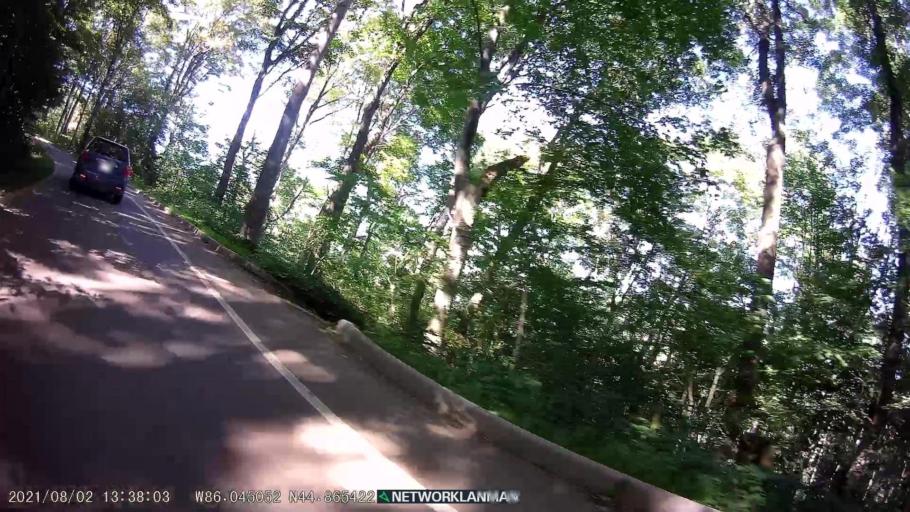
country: US
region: Michigan
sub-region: Benzie County
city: Beulah
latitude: 44.8655
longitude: -86.0451
